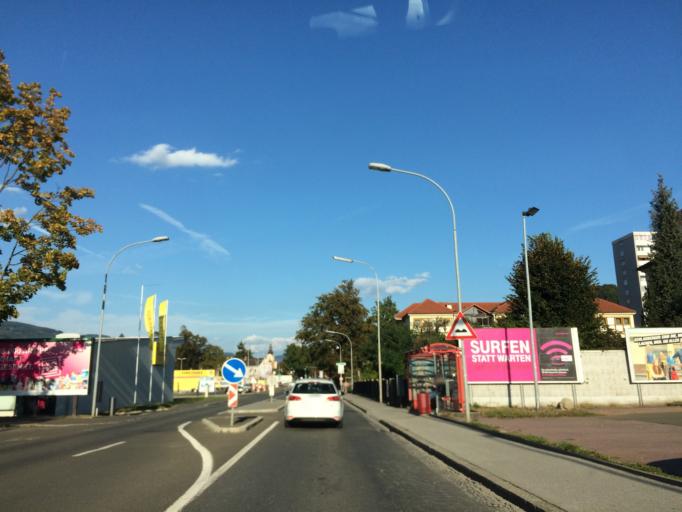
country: AT
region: Styria
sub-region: Politischer Bezirk Leoben
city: Leoben
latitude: 47.3695
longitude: 15.0819
